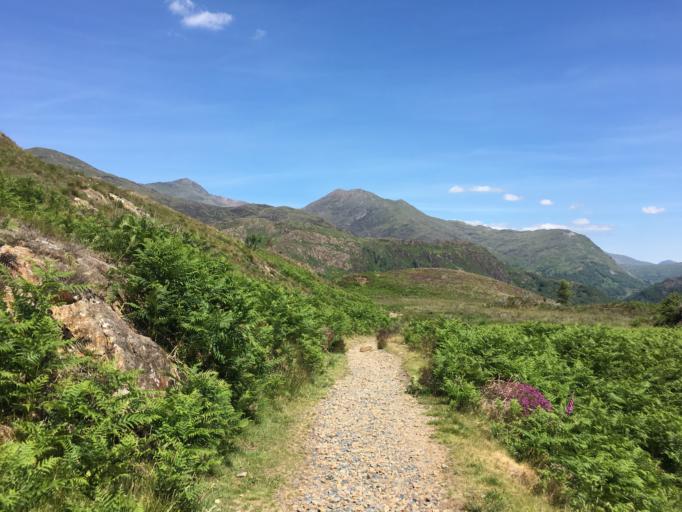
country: GB
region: Wales
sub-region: Gwynedd
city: Penrhyndeudraeth
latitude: 53.0171
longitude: -4.0711
